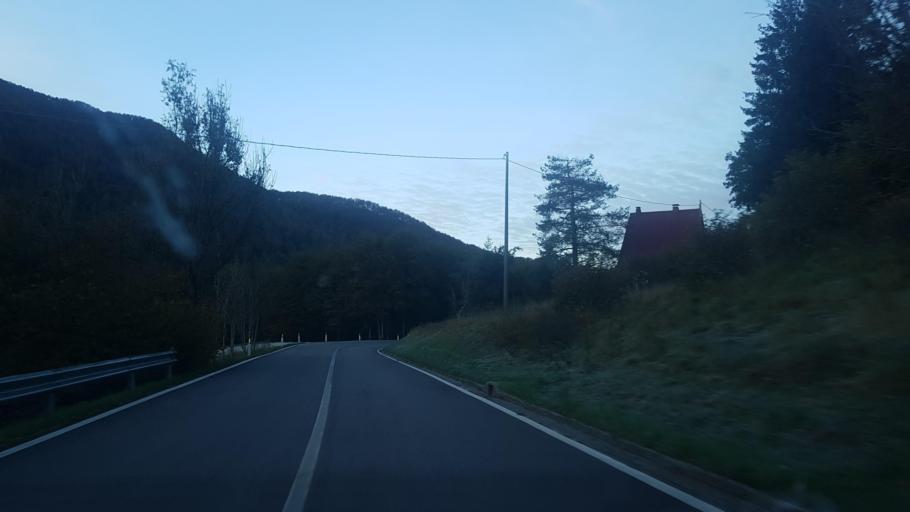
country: IT
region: Friuli Venezia Giulia
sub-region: Provincia di Udine
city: Villa Santina
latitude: 46.3573
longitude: 12.9349
